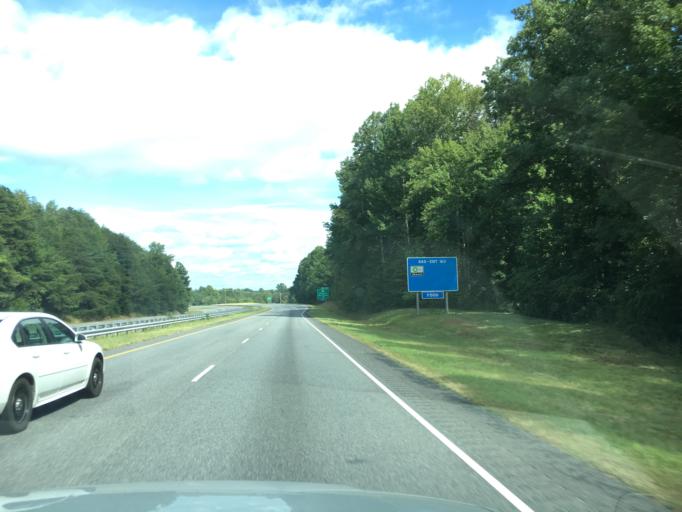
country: US
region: North Carolina
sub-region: Polk County
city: Columbus
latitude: 35.2592
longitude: -82.1901
